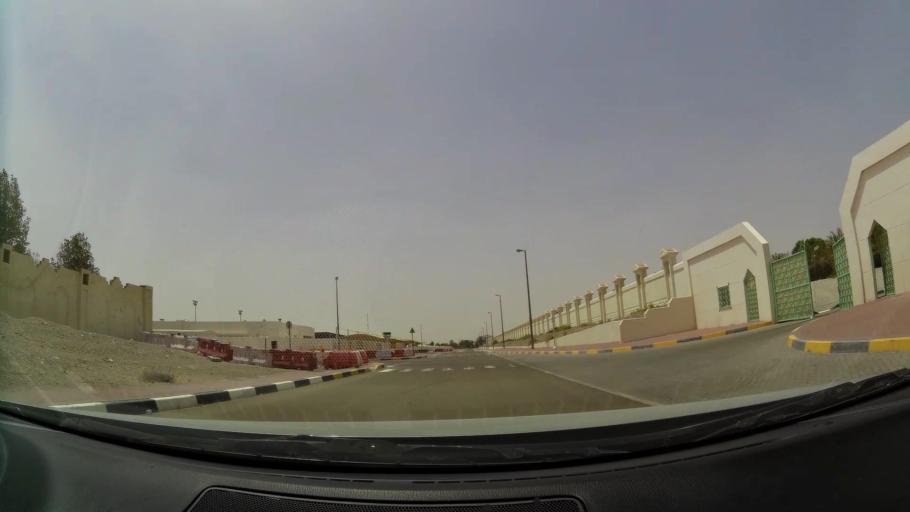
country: AE
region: Abu Dhabi
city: Al Ain
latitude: 24.1917
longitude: 55.6894
